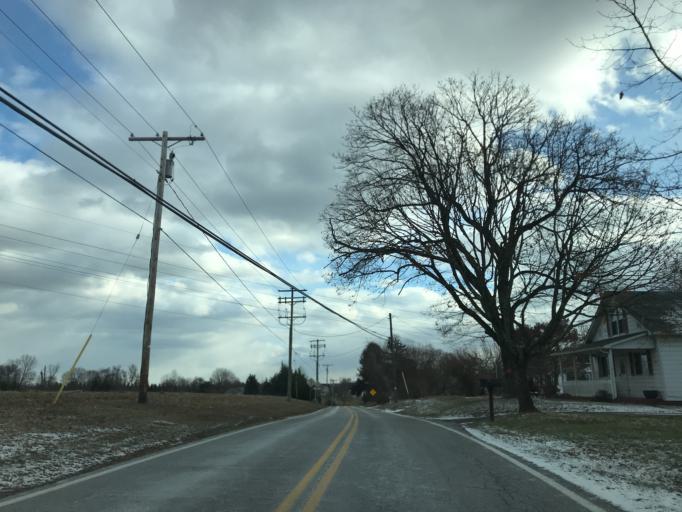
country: US
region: Maryland
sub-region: Harford County
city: Jarrettsville
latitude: 39.6250
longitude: -76.4557
